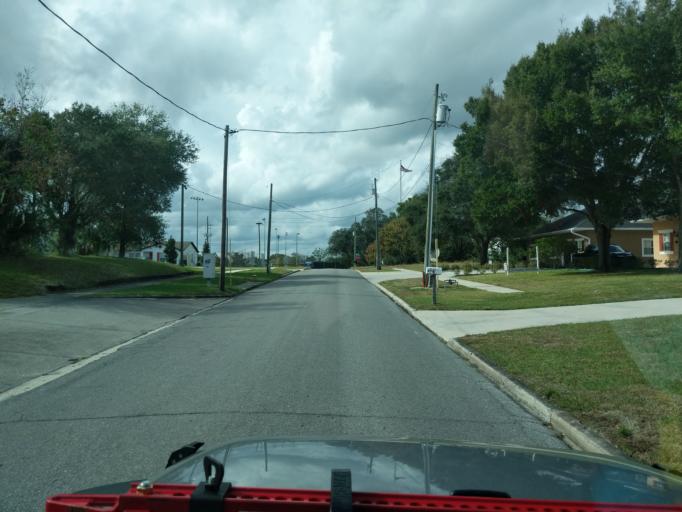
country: US
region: Florida
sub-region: Lake County
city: Clermont
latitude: 28.5563
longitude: -81.7744
